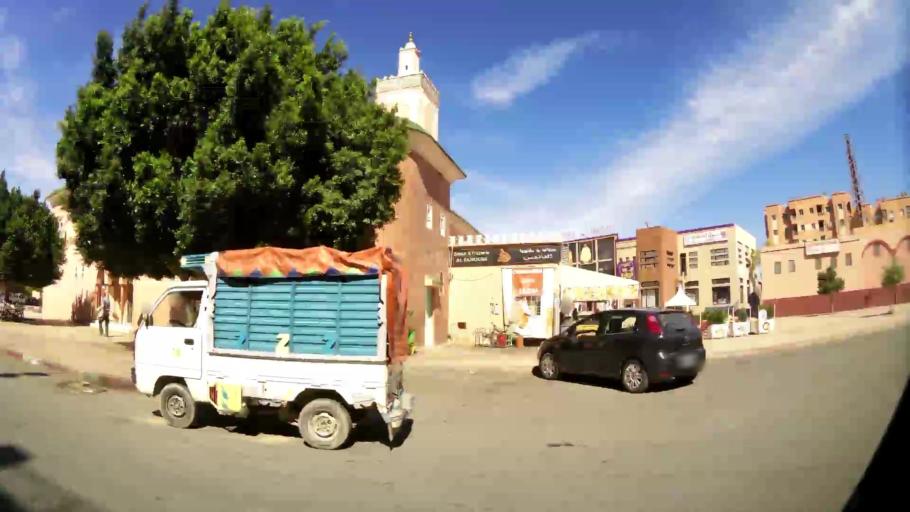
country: MA
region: Marrakech-Tensift-Al Haouz
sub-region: Marrakech
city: Marrakesh
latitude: 31.6755
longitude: -8.0173
